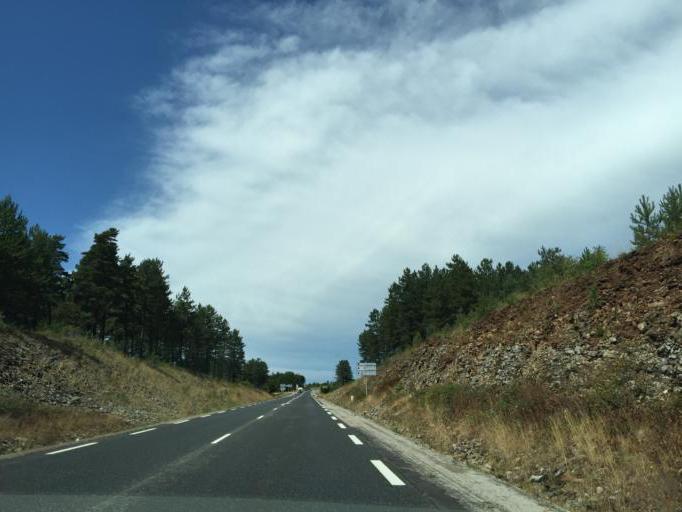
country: FR
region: Midi-Pyrenees
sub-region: Departement de l'Aveyron
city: Millau
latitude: 44.1978
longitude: 3.0188
